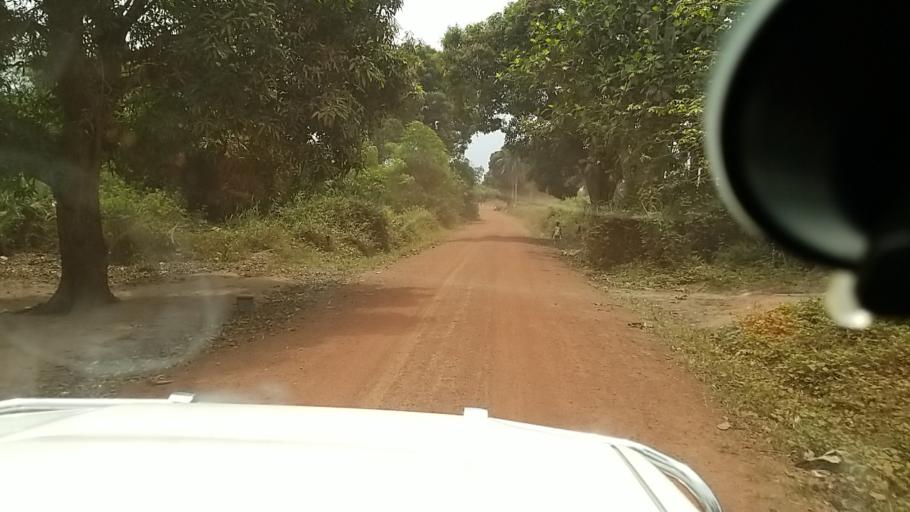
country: CD
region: Equateur
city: Libenge
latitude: 3.7313
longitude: 18.7748
